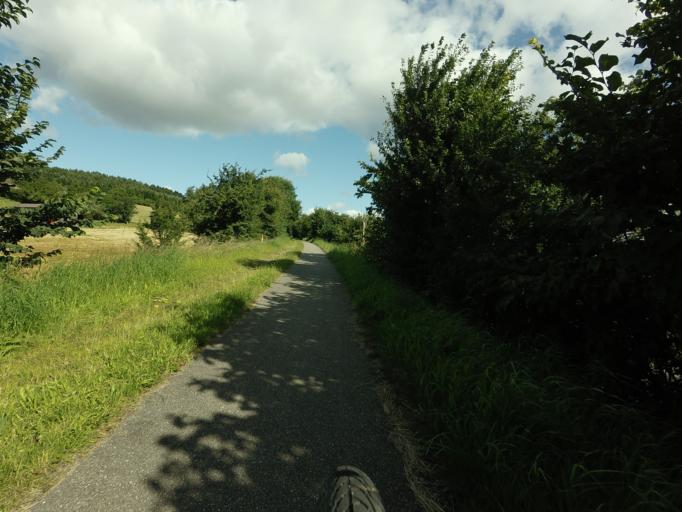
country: DK
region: Central Jutland
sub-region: Horsens Kommune
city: Braedstrup
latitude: 55.9796
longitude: 9.6911
